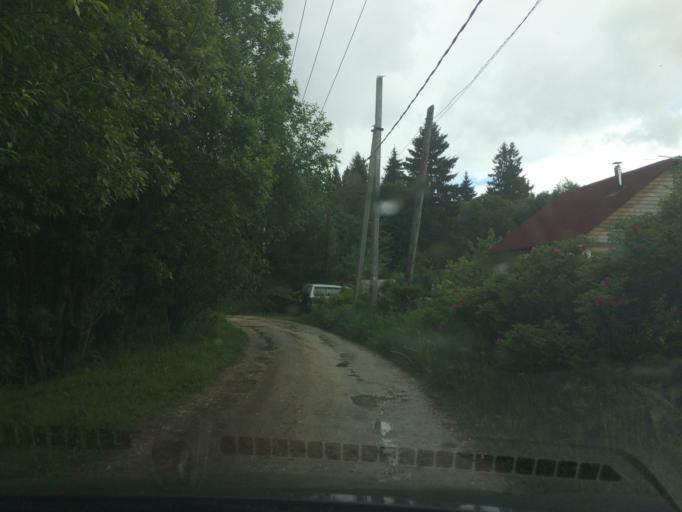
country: RU
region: Moskovskaya
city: Solnechnogorsk
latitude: 56.1609
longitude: 37.0076
